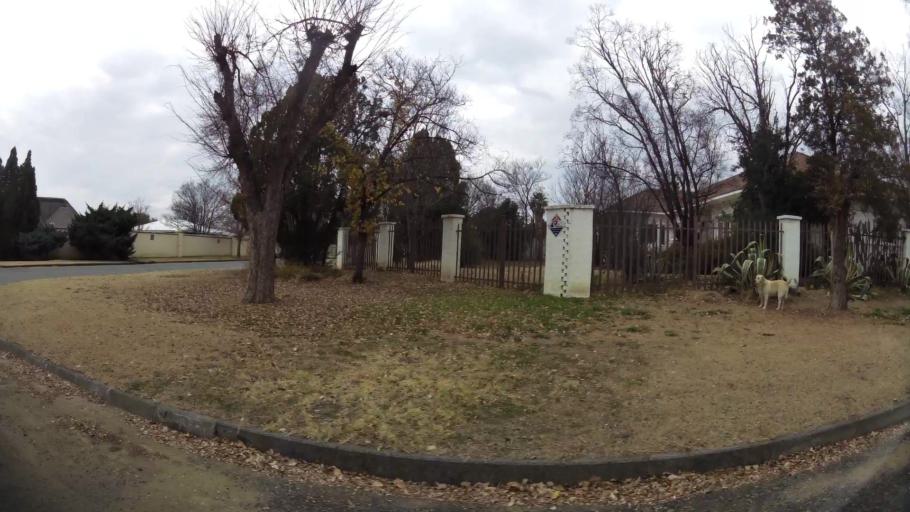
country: ZA
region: Orange Free State
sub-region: Fezile Dabi District Municipality
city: Kroonstad
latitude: -27.6769
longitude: 27.2434
